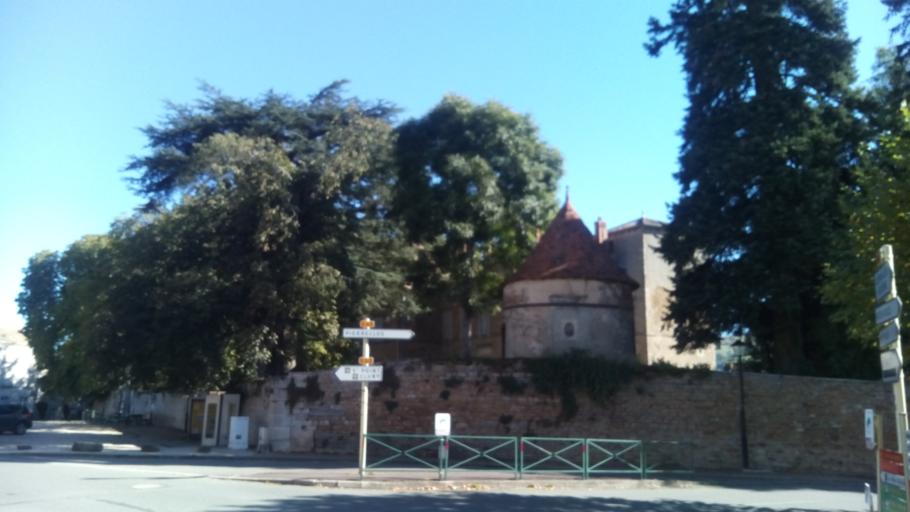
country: FR
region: Bourgogne
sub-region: Departement de Saone-et-Loire
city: Matour
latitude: 46.3067
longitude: 4.6024
